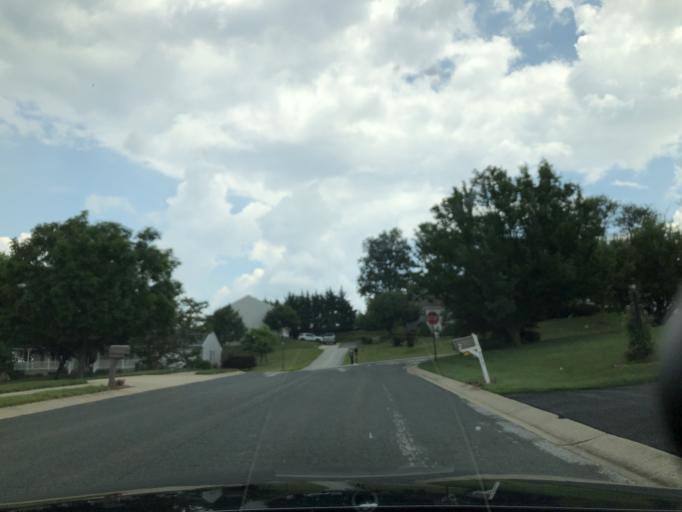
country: US
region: Maryland
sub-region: Carroll County
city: Westminster
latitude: 39.5546
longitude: -76.9792
